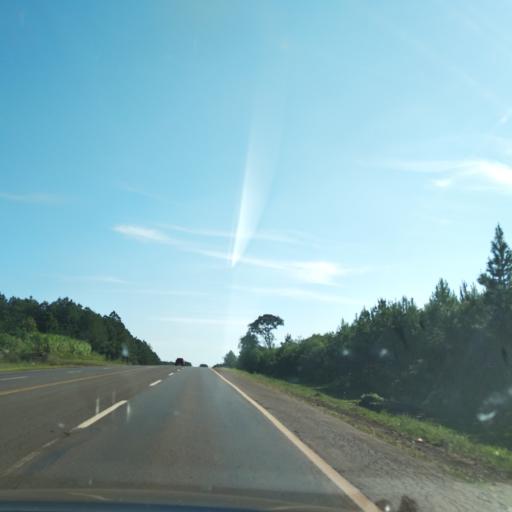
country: AR
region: Misiones
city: Santo Pipo
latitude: -27.1062
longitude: -55.3272
